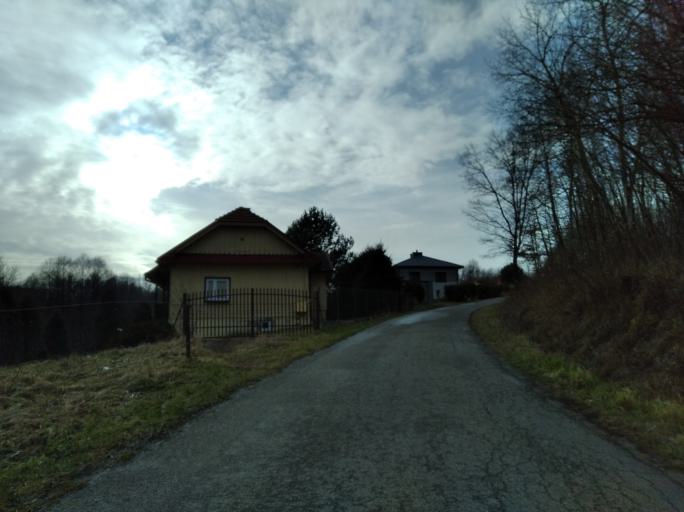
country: PL
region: Subcarpathian Voivodeship
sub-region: Powiat strzyzowski
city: Strzyzow
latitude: 49.8586
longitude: 21.7795
